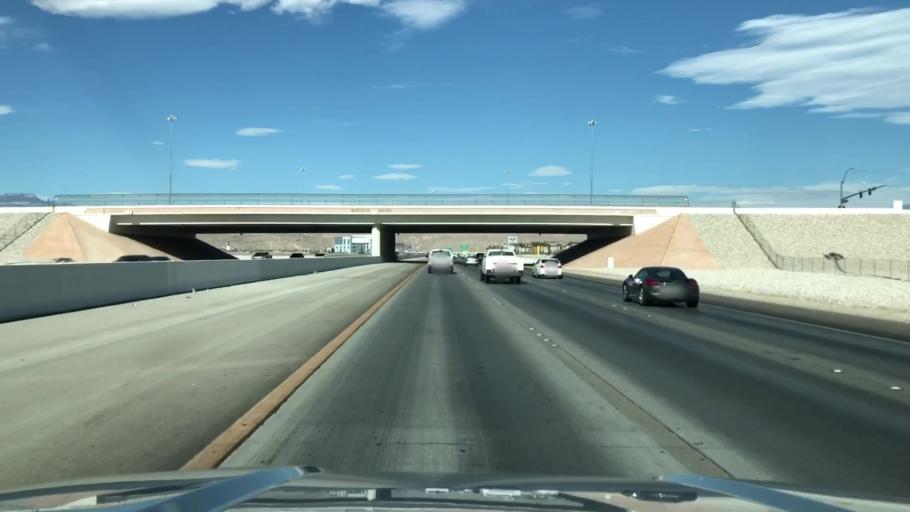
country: US
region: Nevada
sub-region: Clark County
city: Spring Valley
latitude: 36.0663
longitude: -115.2590
